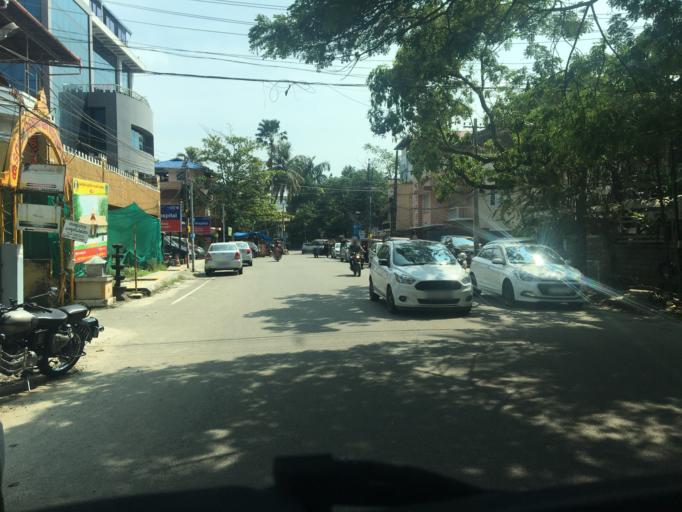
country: IN
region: Kerala
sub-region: Ernakulam
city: Cochin
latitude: 9.9658
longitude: 76.3002
